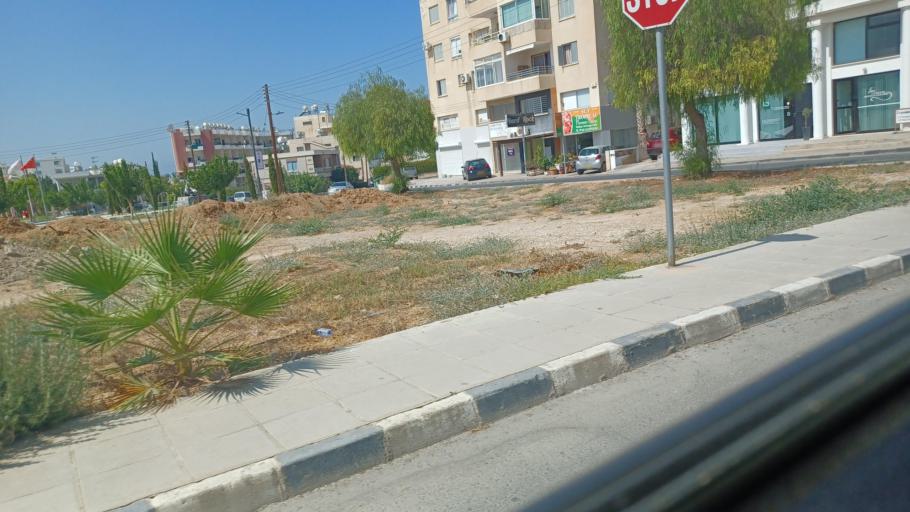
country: CY
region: Pafos
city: Paphos
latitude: 34.7791
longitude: 32.4269
